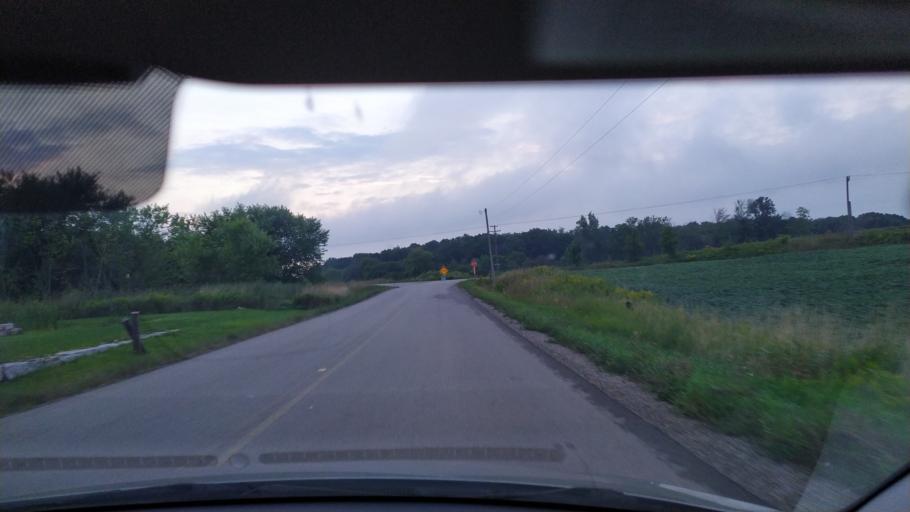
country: CA
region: Ontario
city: Kitchener
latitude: 43.3567
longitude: -80.6495
